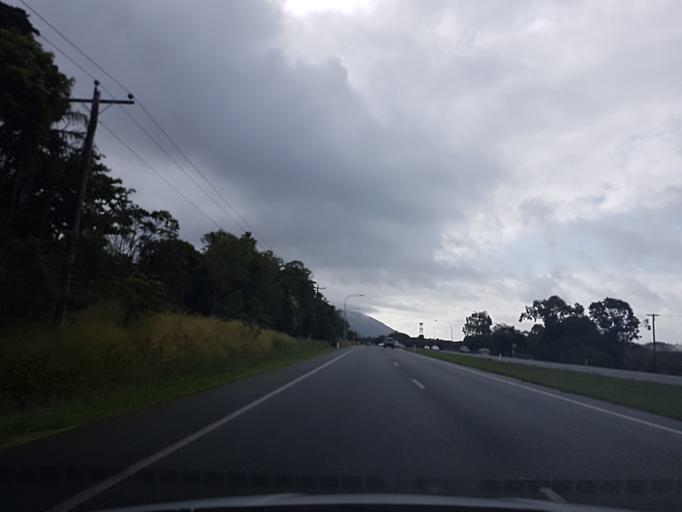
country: AU
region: Queensland
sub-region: Cairns
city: Trinity Beach
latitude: -16.8067
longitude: 145.6911
